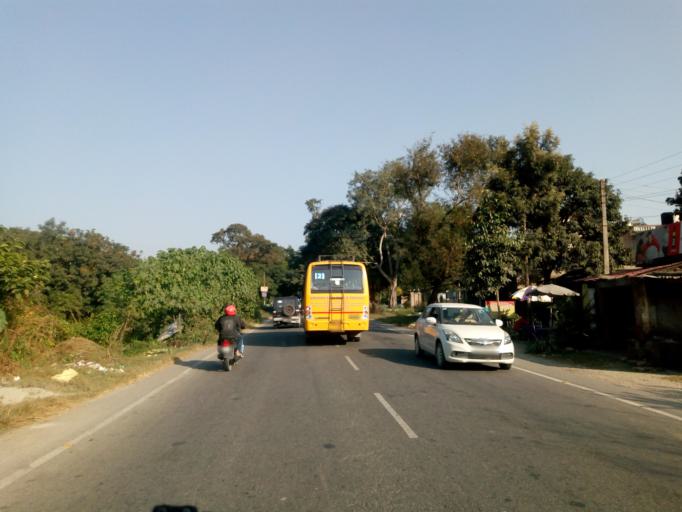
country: IN
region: Uttarakhand
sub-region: Dehradun
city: Dehradun
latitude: 30.3455
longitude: 77.9027
